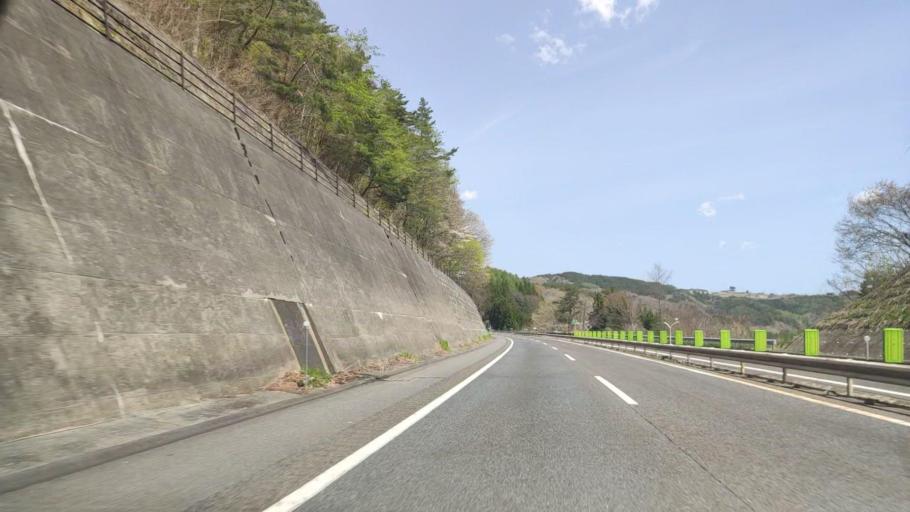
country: JP
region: Aomori
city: Hachinohe
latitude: 40.3568
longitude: 141.4499
